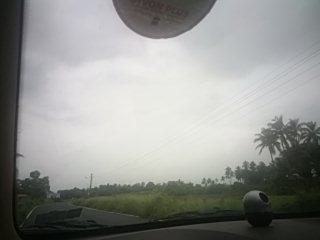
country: IN
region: Goa
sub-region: South Goa
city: Cavelossim
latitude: 15.1811
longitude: 73.9567
